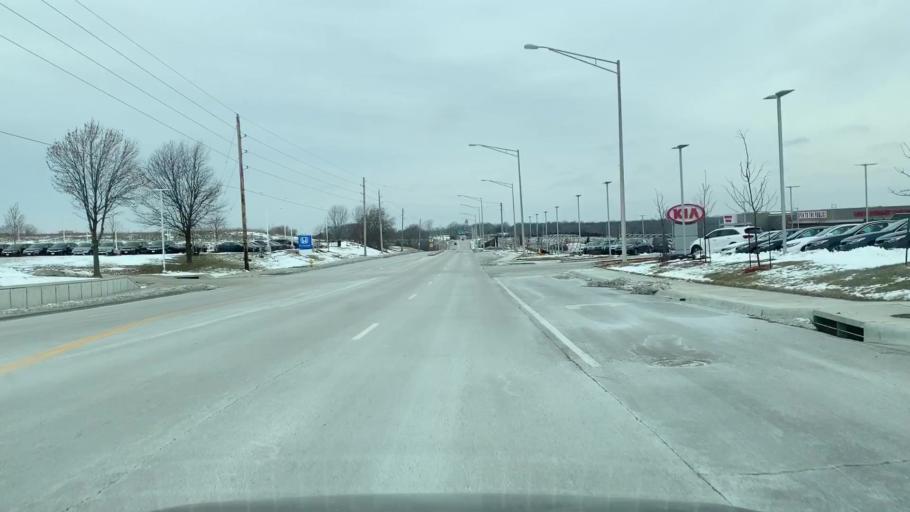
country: US
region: Missouri
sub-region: Jackson County
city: Lees Summit
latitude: 38.9465
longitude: -94.3704
